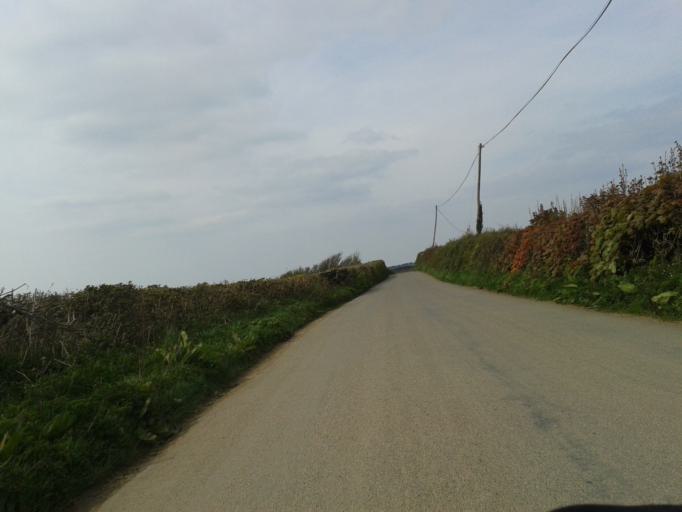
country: GB
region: England
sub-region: Devon
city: Braunton
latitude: 51.1215
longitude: -4.1772
